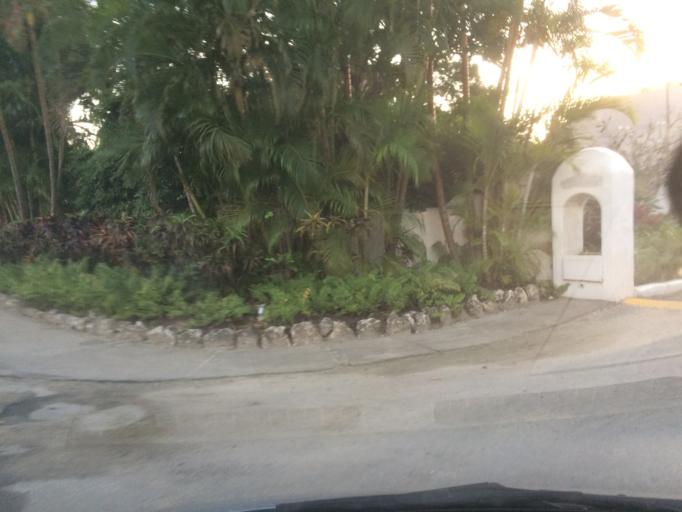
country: BB
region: Saint James
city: Holetown
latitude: 13.2118
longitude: -59.6397
